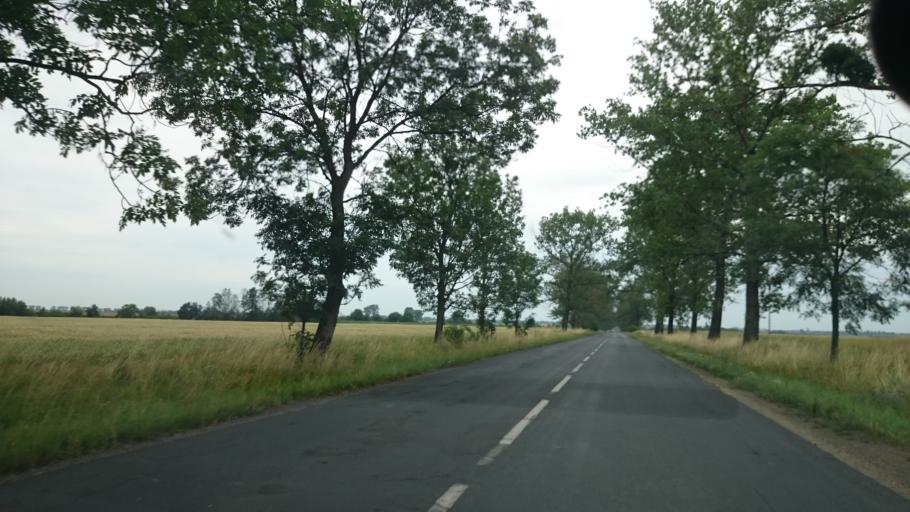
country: PL
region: Opole Voivodeship
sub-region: Powiat brzeski
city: Grodkow
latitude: 50.6794
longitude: 17.3356
